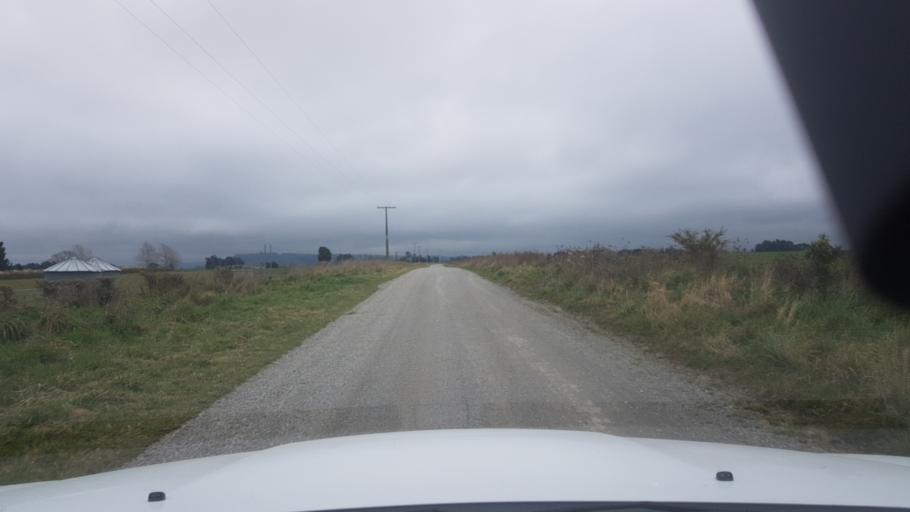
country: NZ
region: Canterbury
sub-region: Timaru District
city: Timaru
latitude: -44.4229
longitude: 171.1725
